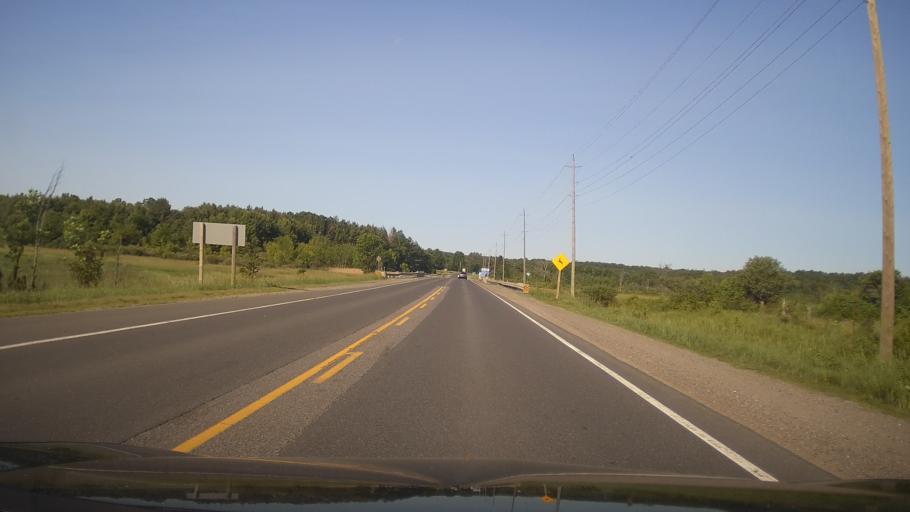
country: CA
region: Ontario
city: Quinte West
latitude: 44.5080
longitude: -77.4895
